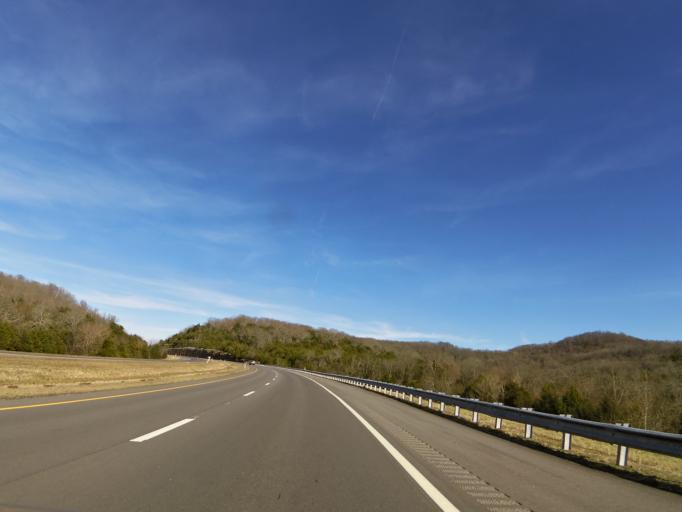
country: US
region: Tennessee
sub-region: Cannon County
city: Woodbury
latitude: 35.8050
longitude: -86.1387
